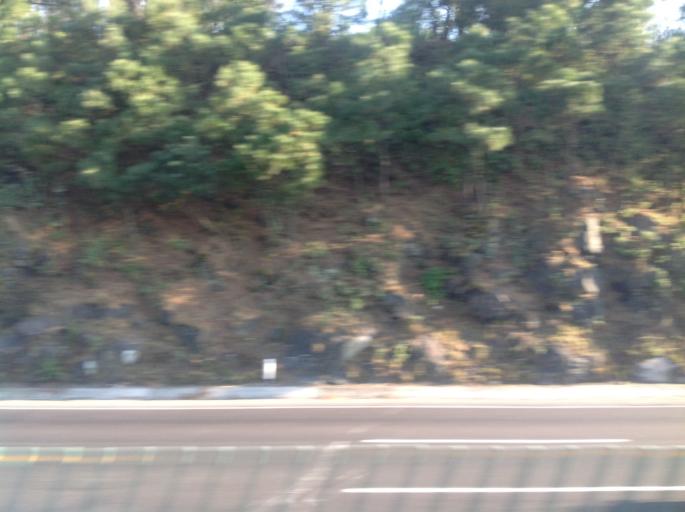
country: MX
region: Mexico
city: Rio Frio de Juarez
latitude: 19.3168
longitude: -98.7362
